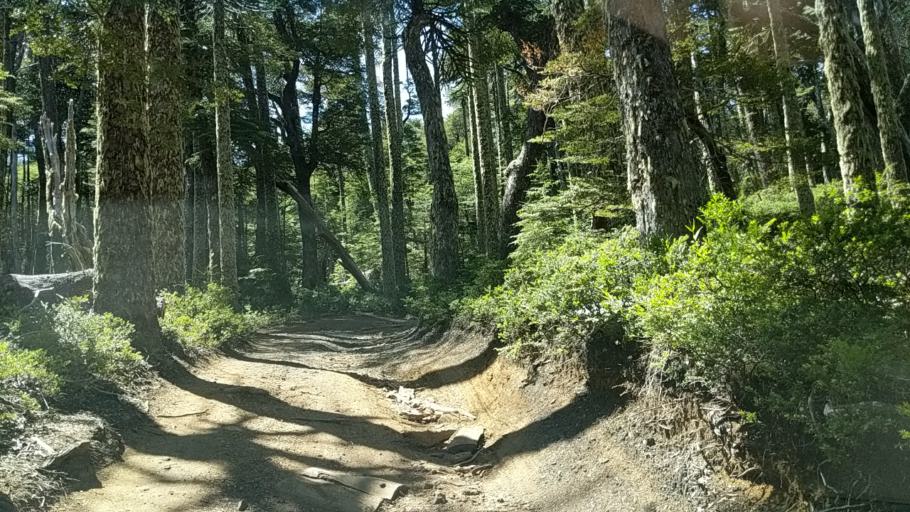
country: CL
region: Araucania
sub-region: Provincia de Cautin
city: Pucon
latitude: -39.4633
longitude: -71.8514
